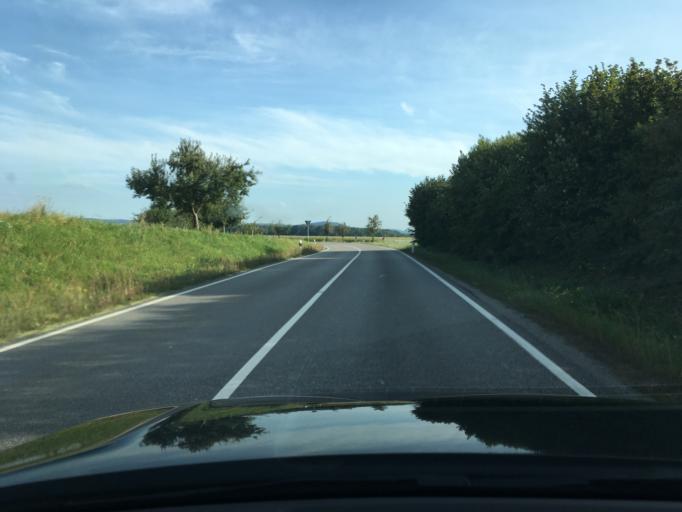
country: DE
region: Baden-Wuerttemberg
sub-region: Regierungsbezirk Stuttgart
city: Affalterbach
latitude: 48.9157
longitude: 9.3335
